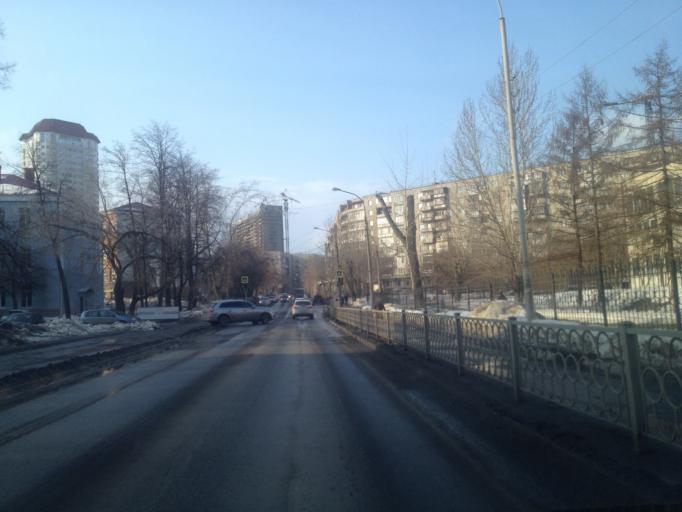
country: RU
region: Sverdlovsk
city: Yekaterinburg
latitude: 56.8515
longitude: 60.5858
